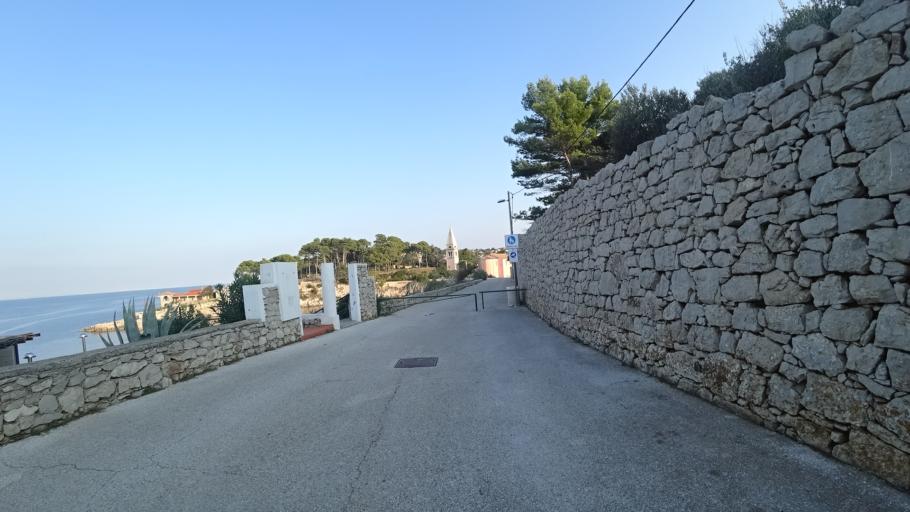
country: HR
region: Primorsko-Goranska
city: Mali Losinj
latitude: 44.5238
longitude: 14.4989
